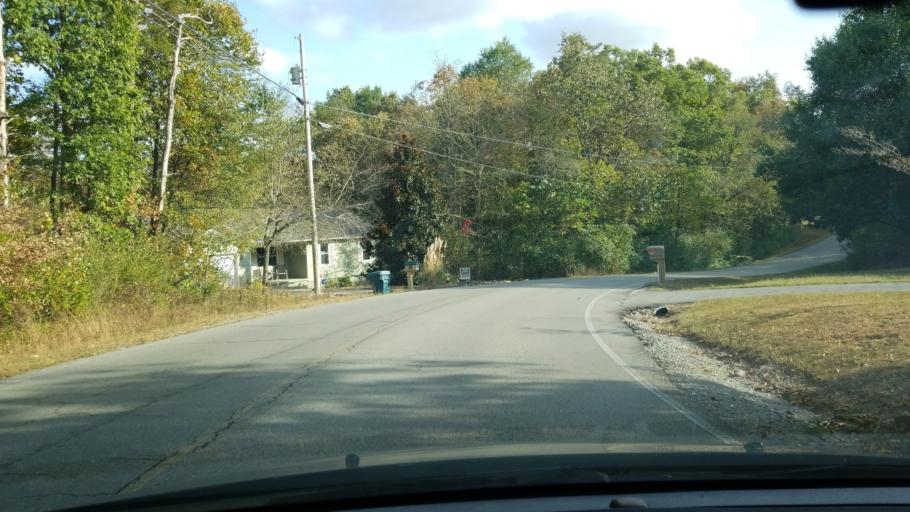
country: US
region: Tennessee
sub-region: Cumberland County
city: Crossville
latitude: 35.9541
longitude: -85.0549
